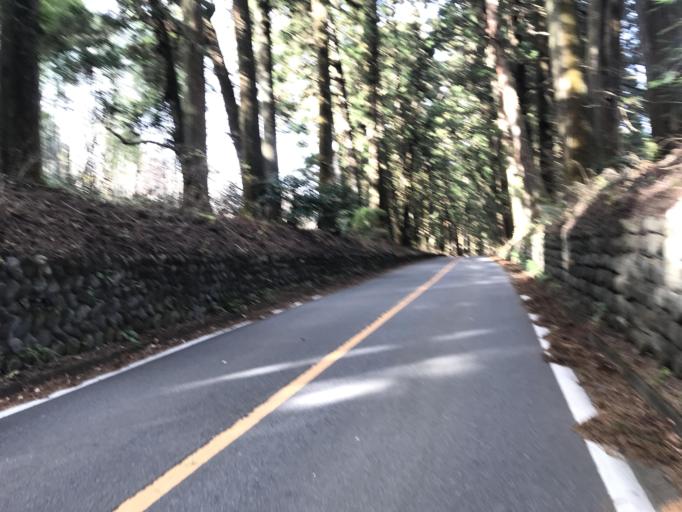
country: JP
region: Tochigi
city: Imaichi
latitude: 36.6926
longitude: 139.7153
